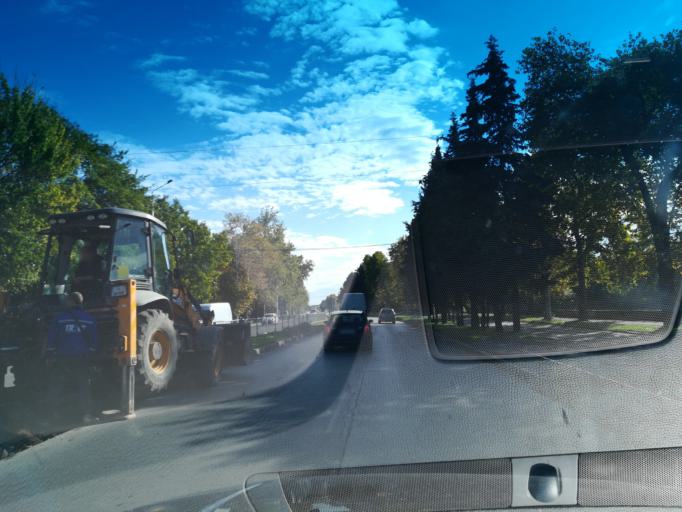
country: BG
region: Stara Zagora
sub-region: Obshtina Stara Zagora
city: Stara Zagora
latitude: 42.4083
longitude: 25.6402
